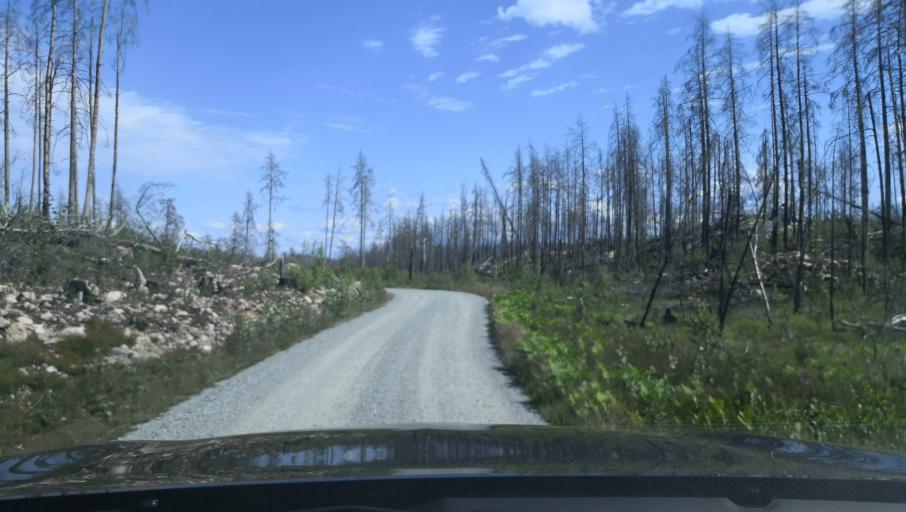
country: SE
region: Vaestmanland
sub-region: Surahammars Kommun
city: Ramnas
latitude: 59.9299
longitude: 16.1796
